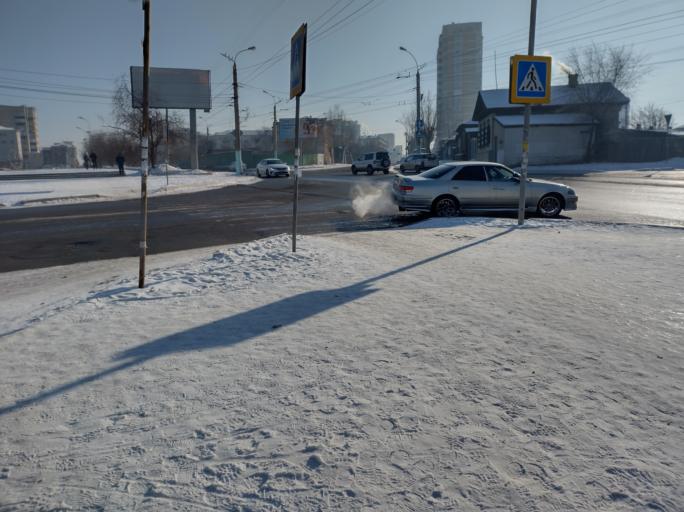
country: RU
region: Transbaikal Territory
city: Chita
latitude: 52.0385
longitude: 113.4884
